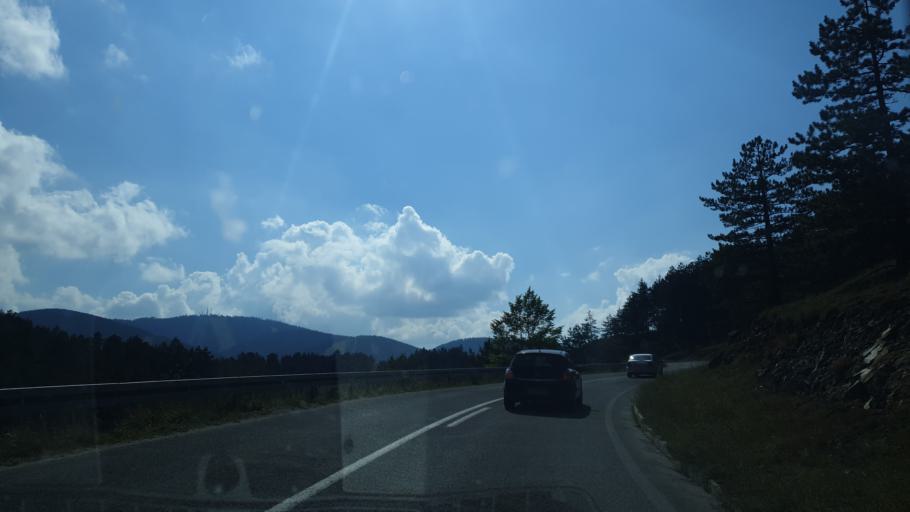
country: RS
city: Zlatibor
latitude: 43.6851
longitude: 19.6600
